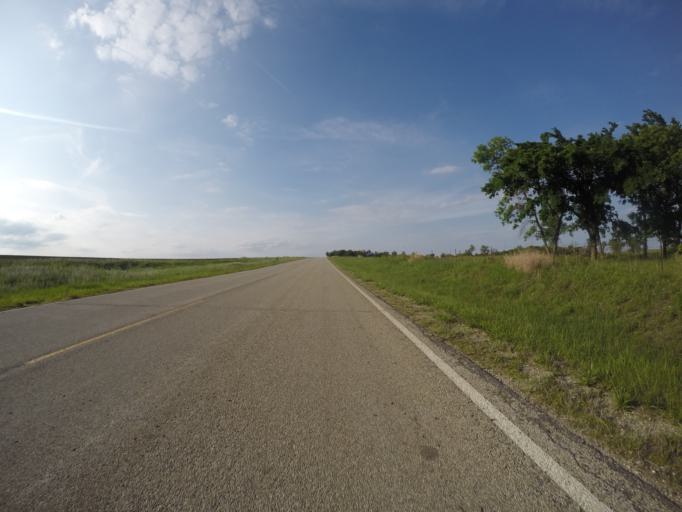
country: US
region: Kansas
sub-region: Pottawatomie County
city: Westmoreland
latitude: 39.4229
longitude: -96.6069
